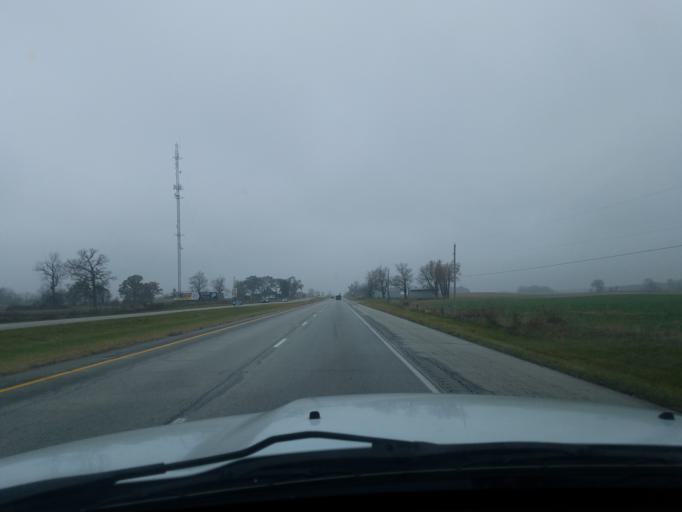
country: US
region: Indiana
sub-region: Hamilton County
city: Arcadia
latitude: 40.1959
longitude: -86.1281
